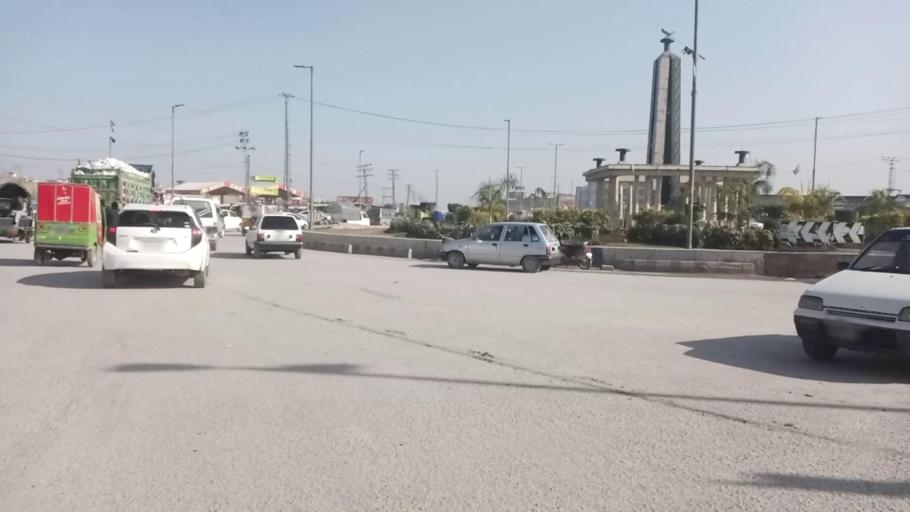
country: PK
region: Khyber Pakhtunkhwa
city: Peshawar
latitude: 34.0323
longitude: 71.6064
